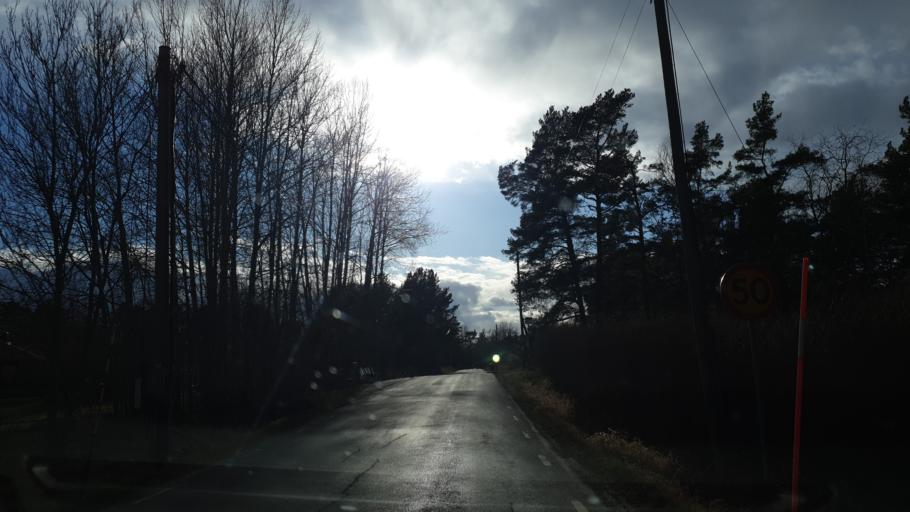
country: SE
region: Stockholm
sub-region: Varmdo Kommun
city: Holo
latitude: 59.3593
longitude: 18.6667
